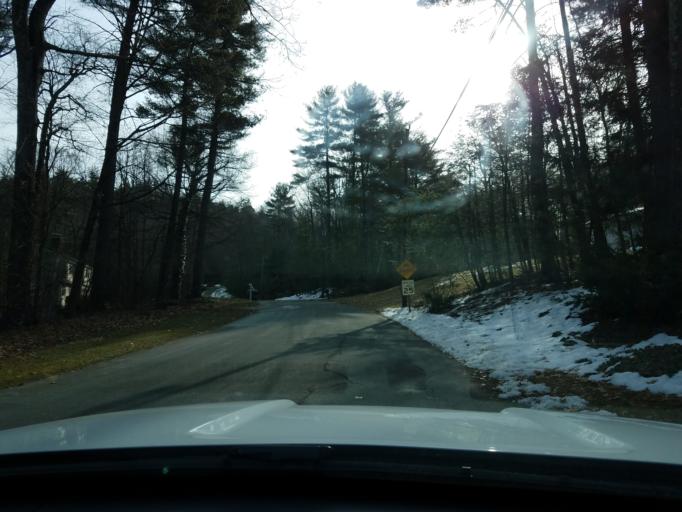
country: US
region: Connecticut
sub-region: Hartford County
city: Canton Valley
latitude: 41.8069
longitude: -72.8775
